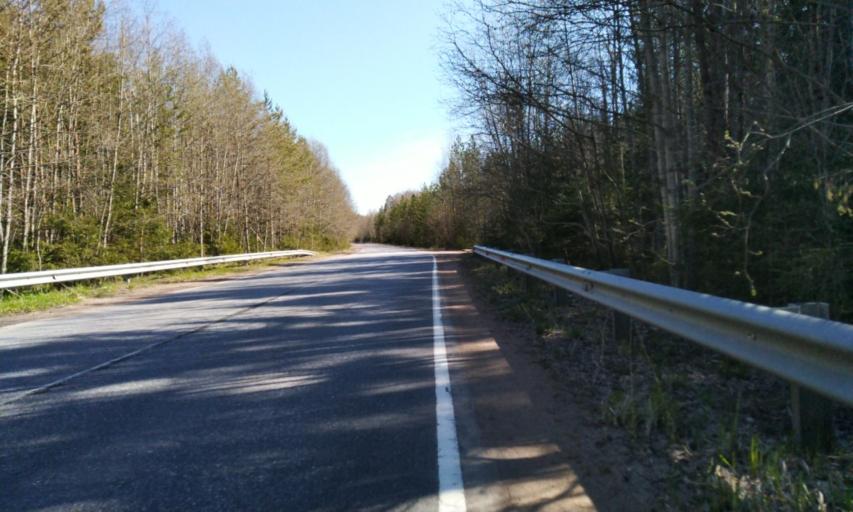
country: RU
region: Leningrad
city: Garbolovo
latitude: 60.3761
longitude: 30.4563
